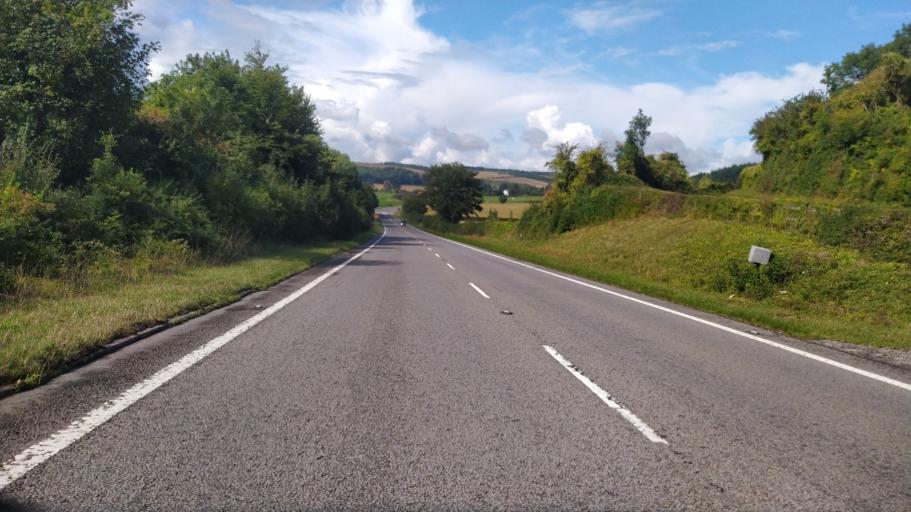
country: GB
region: England
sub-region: Dorset
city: Blandford Forum
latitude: 50.8731
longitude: -2.1716
